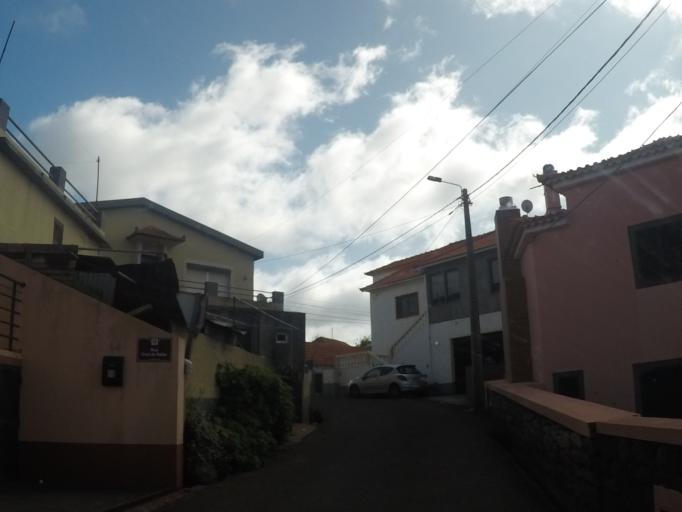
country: PT
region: Madeira
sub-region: Calheta
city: Faja da Ovelha
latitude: 32.8137
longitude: -17.2461
